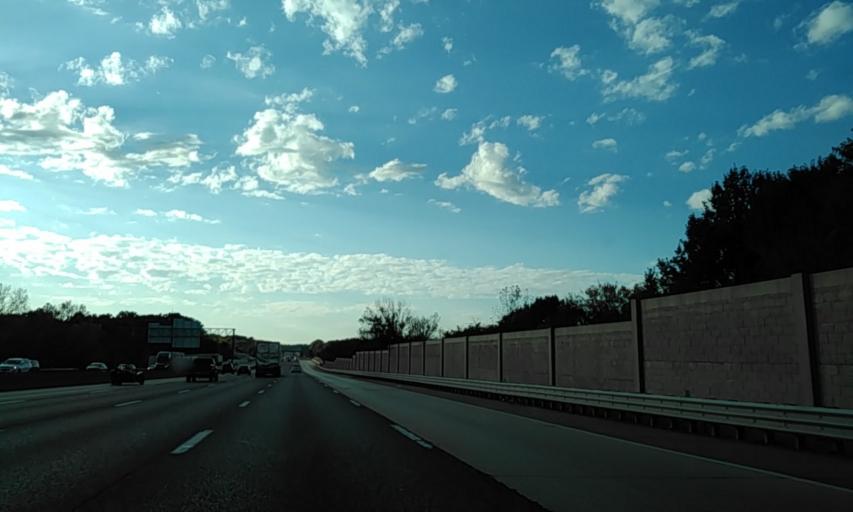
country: US
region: Missouri
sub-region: Saint Louis County
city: Concord
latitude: 38.5105
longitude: -90.3613
